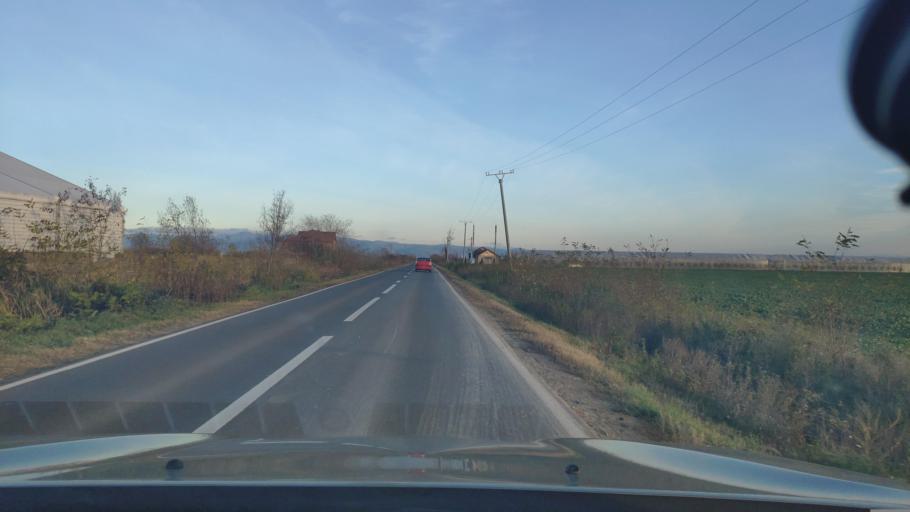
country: RO
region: Satu Mare
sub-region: Comuna Mediesu Aurit
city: Potau
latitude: 47.7729
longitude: 23.1252
